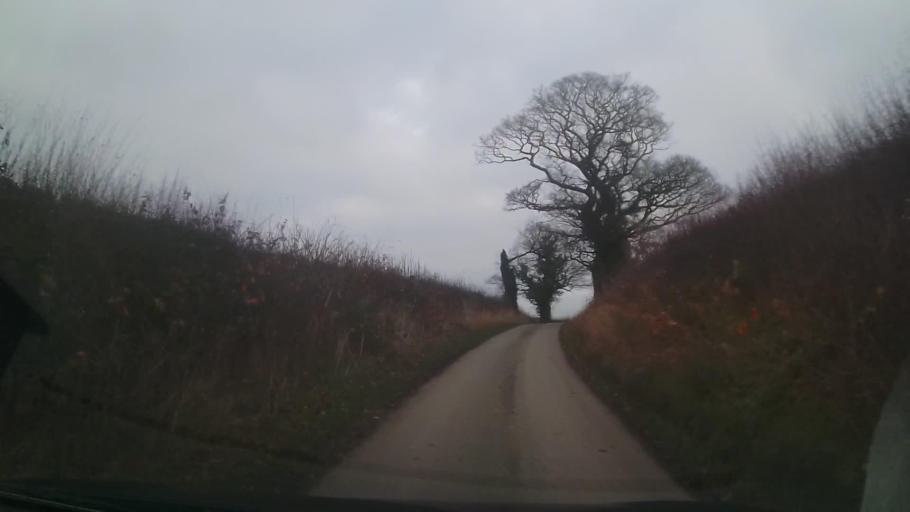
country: GB
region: England
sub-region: Shropshire
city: Petton
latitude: 52.8029
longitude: -2.8073
